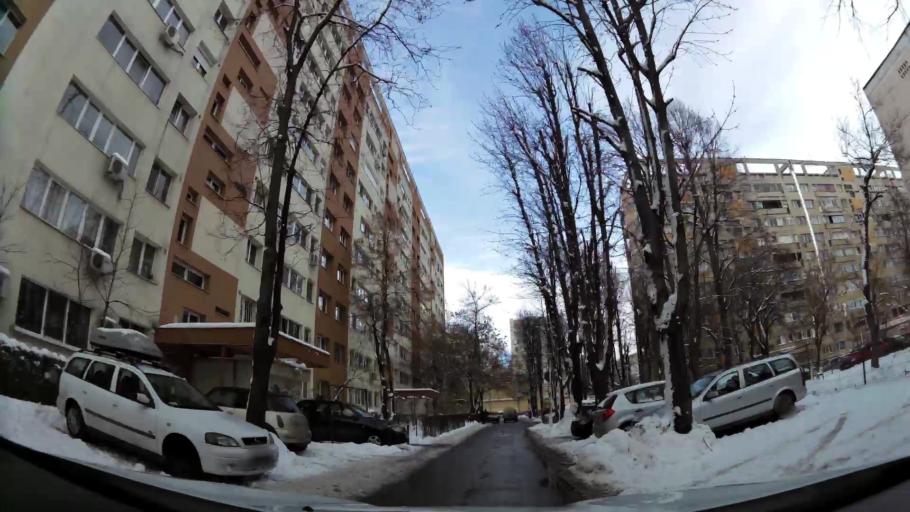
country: RO
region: Ilfov
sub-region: Comuna Popesti-Leordeni
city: Popesti-Leordeni
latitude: 44.3810
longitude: 26.1174
